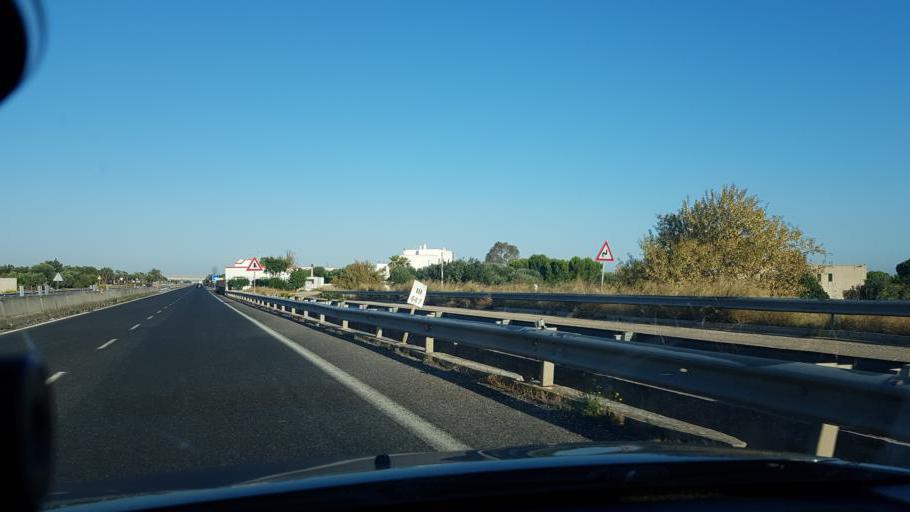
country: IT
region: Apulia
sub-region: Provincia di Bari
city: Monopoli
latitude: 40.9265
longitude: 17.3100
